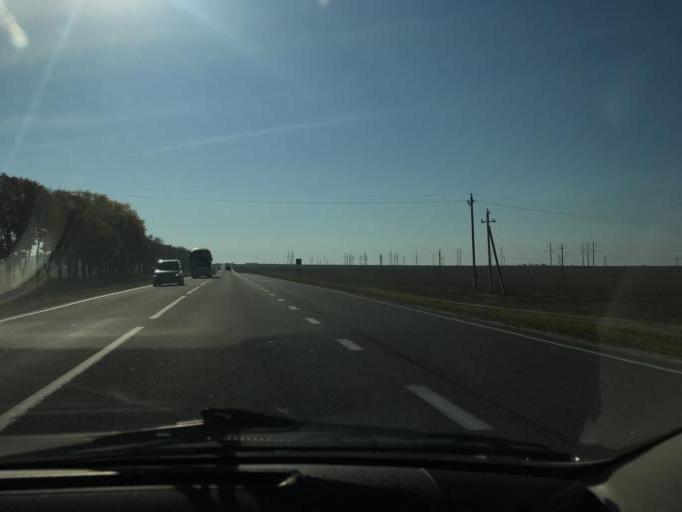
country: BY
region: Minsk
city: Salihorsk
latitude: 52.8696
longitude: 27.4672
